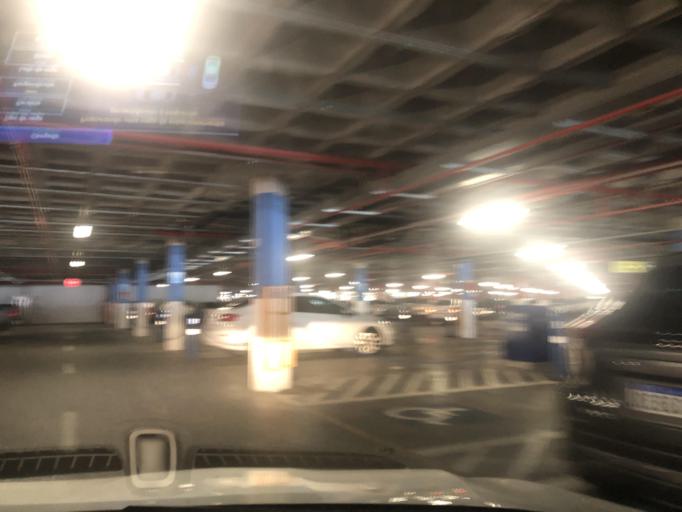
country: BR
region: Santa Catarina
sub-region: Lages
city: Lages
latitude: -27.7932
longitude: -50.2837
